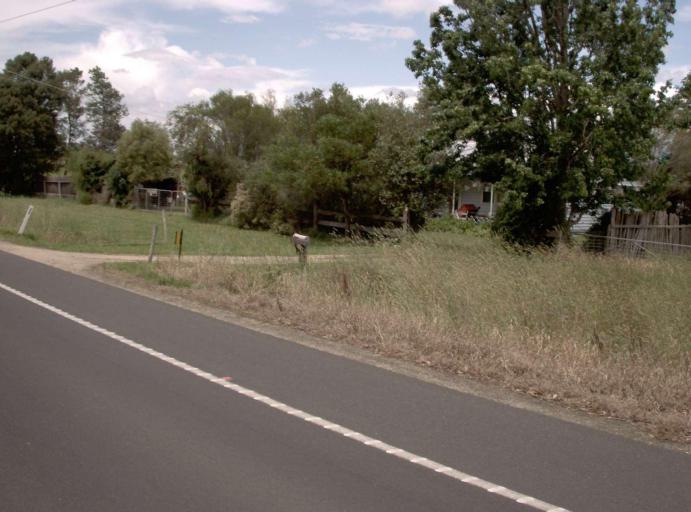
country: AU
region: Victoria
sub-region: Wellington
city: Sale
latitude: -38.0312
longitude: 147.0151
